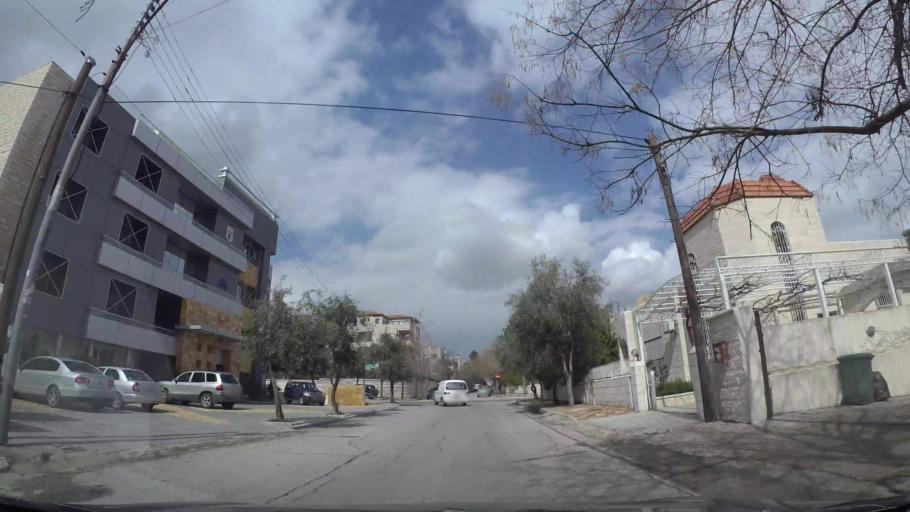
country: JO
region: Amman
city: Amman
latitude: 31.9721
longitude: 35.8995
